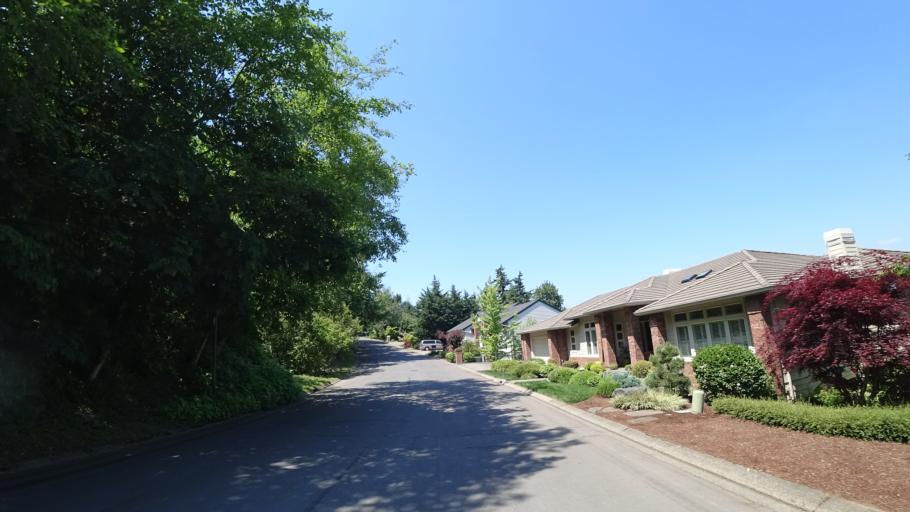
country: US
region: Oregon
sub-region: Washington County
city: Metzger
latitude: 45.4392
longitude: -122.7197
